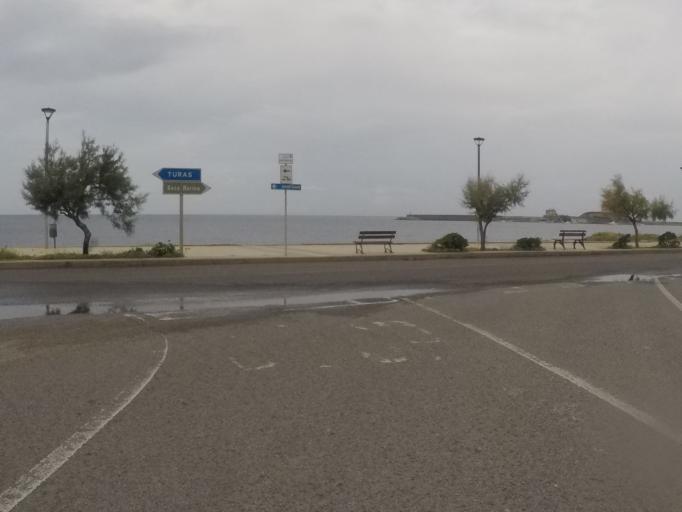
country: IT
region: Sardinia
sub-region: Provincia di Oristano
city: Bosa
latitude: 40.2839
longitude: 8.4836
